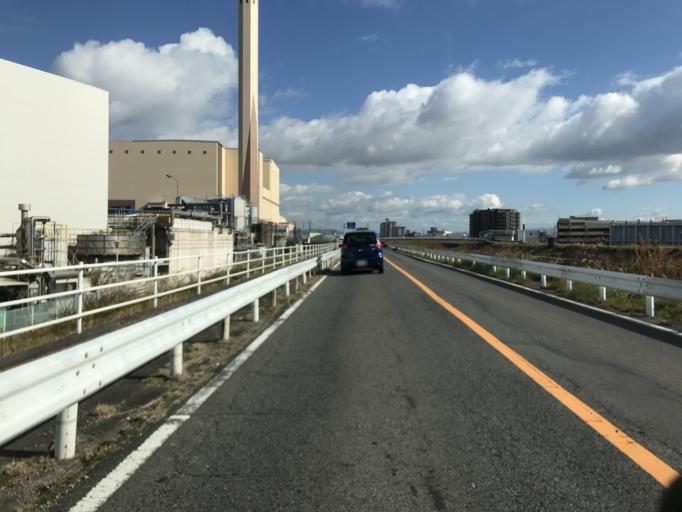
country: JP
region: Aichi
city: Nagoya-shi
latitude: 35.2280
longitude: 136.8819
